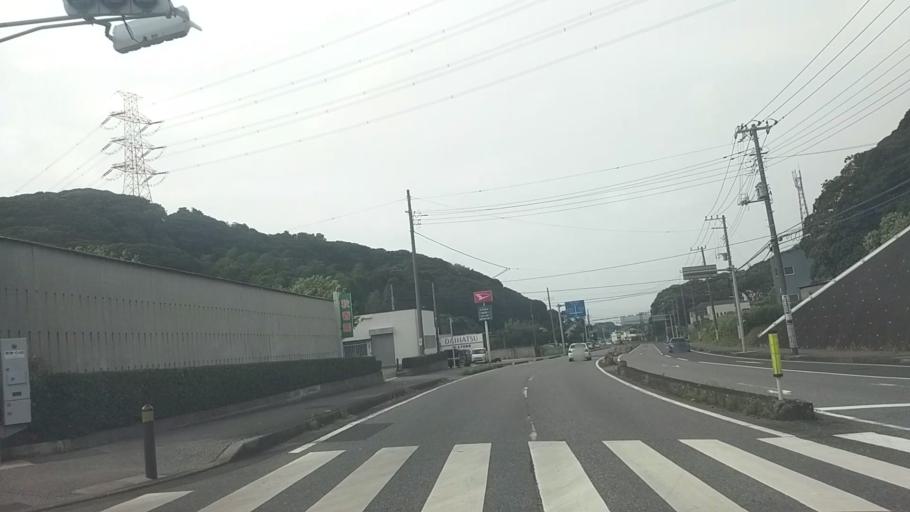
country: JP
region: Chiba
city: Kimitsu
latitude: 35.3434
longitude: 139.8904
